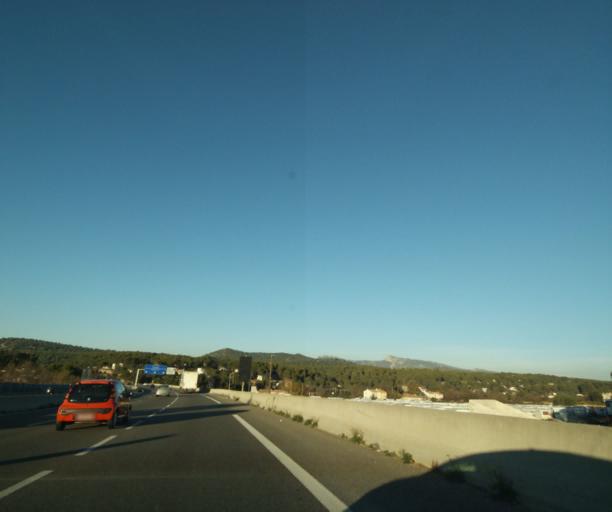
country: FR
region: Provence-Alpes-Cote d'Azur
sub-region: Departement des Bouches-du-Rhone
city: Roquefort-la-Bedoule
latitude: 43.2453
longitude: 5.5960
